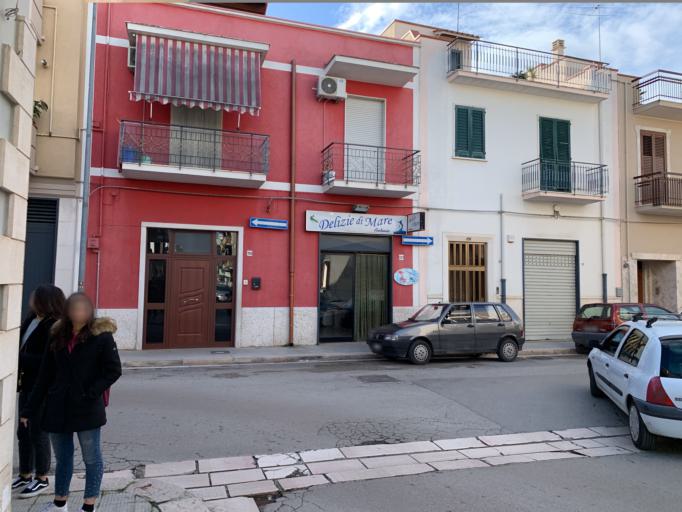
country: IT
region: Apulia
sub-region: Provincia di Barletta - Andria - Trani
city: Andria
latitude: 41.2314
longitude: 16.2914
